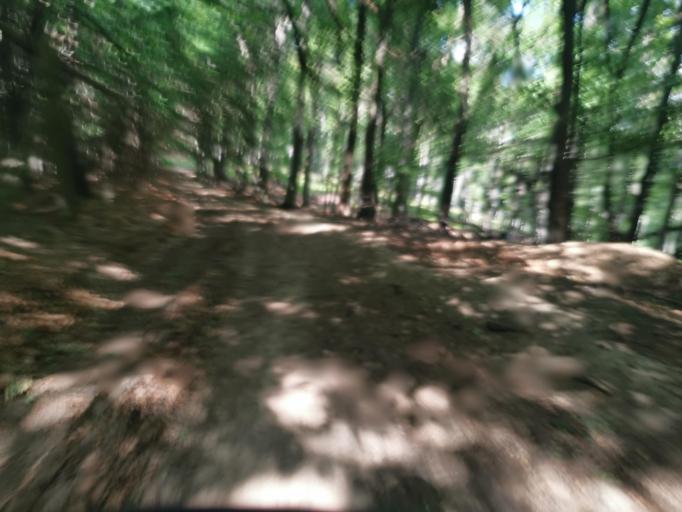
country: CZ
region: South Moravian
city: Knezdub
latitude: 48.8151
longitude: 17.3994
